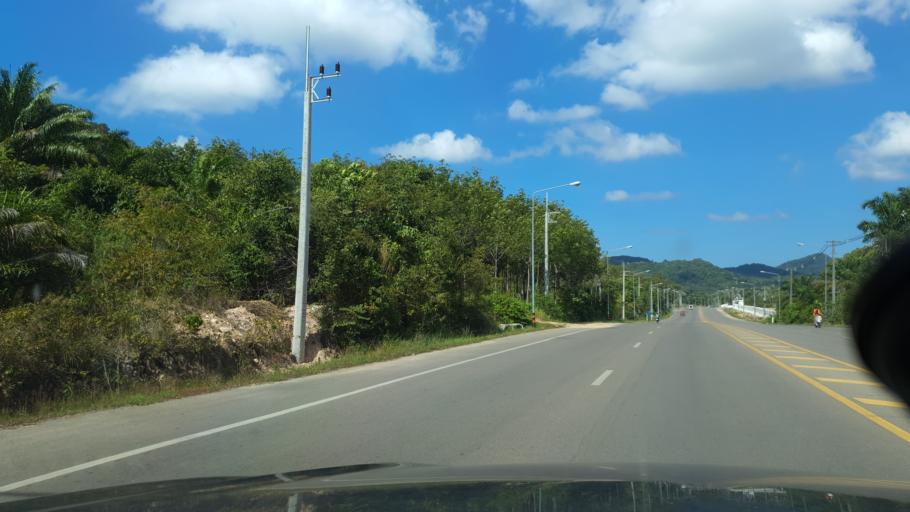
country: TH
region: Phangnga
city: Ban Ao Nang
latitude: 8.0380
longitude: 98.8534
